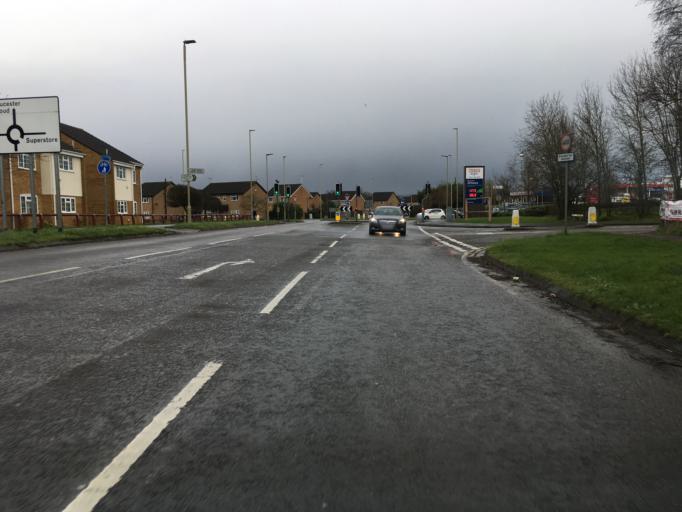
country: GB
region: England
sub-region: Gloucestershire
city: Gloucester
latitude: 51.8288
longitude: -2.2814
